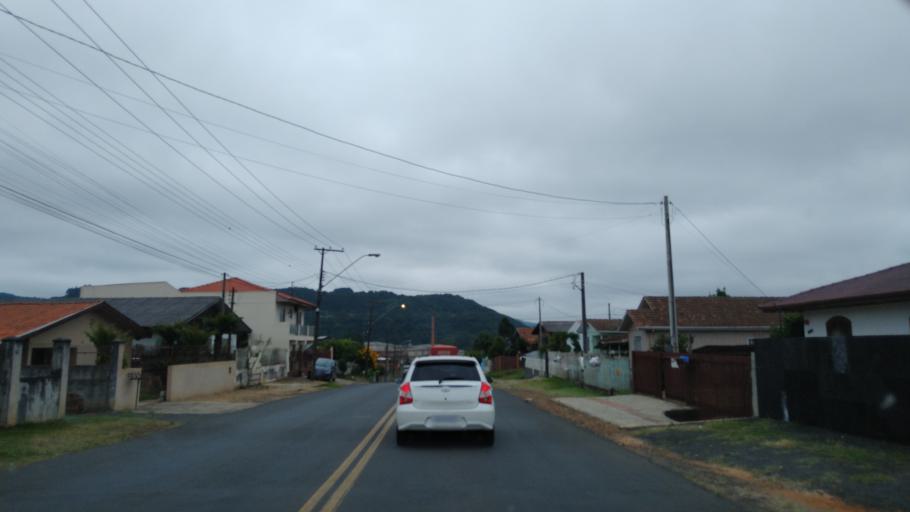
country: BR
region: Santa Catarina
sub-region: Porto Uniao
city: Porto Uniao
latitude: -26.2539
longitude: -51.0910
